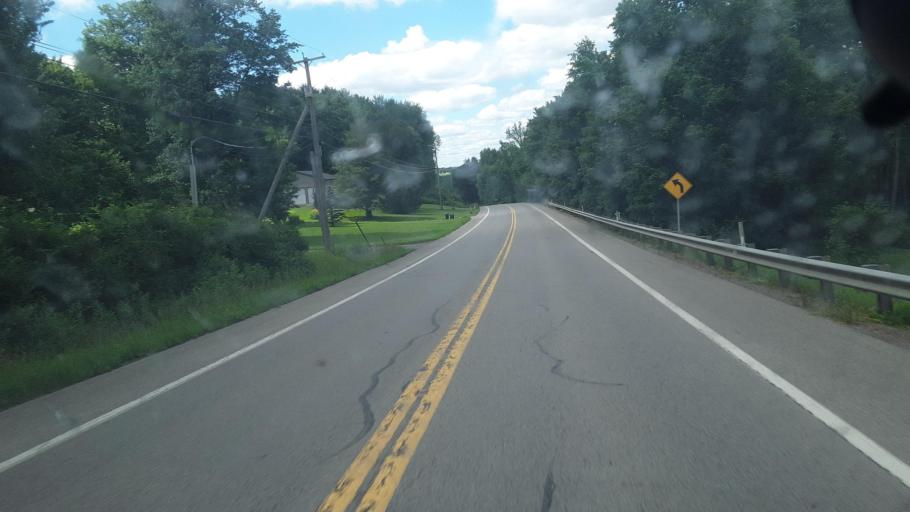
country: US
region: Pennsylvania
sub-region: Butler County
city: Slippery Rock
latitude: 40.9982
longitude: -80.1706
